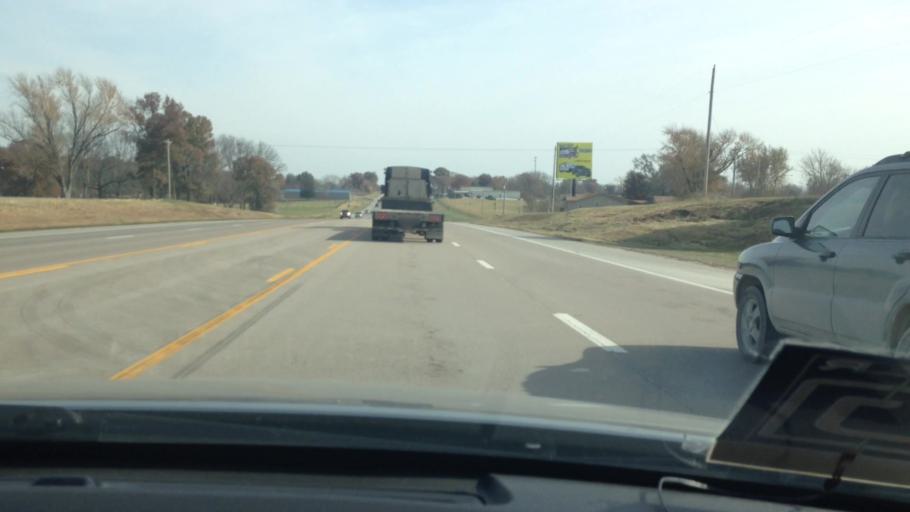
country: US
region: Missouri
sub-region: Henry County
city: Clinton
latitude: 38.3898
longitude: -93.8173
